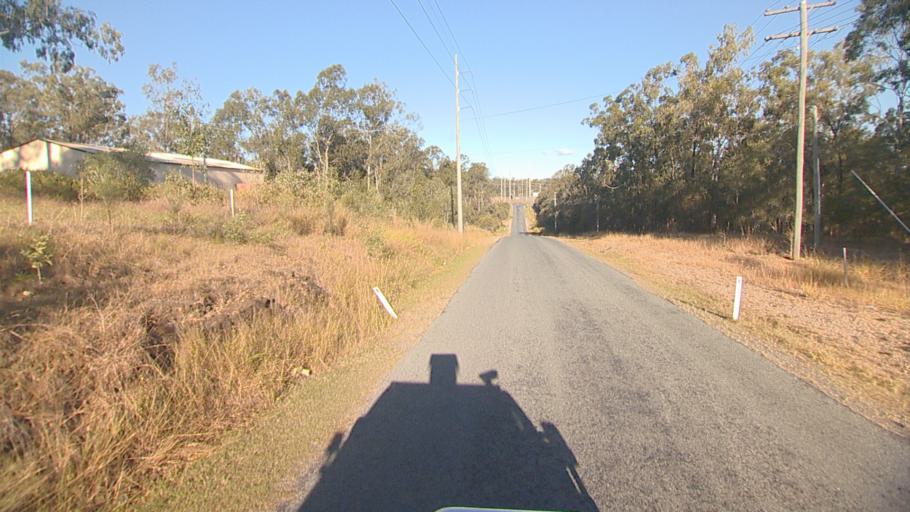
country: AU
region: Queensland
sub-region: Logan
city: North Maclean
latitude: -27.8062
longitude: 153.0422
